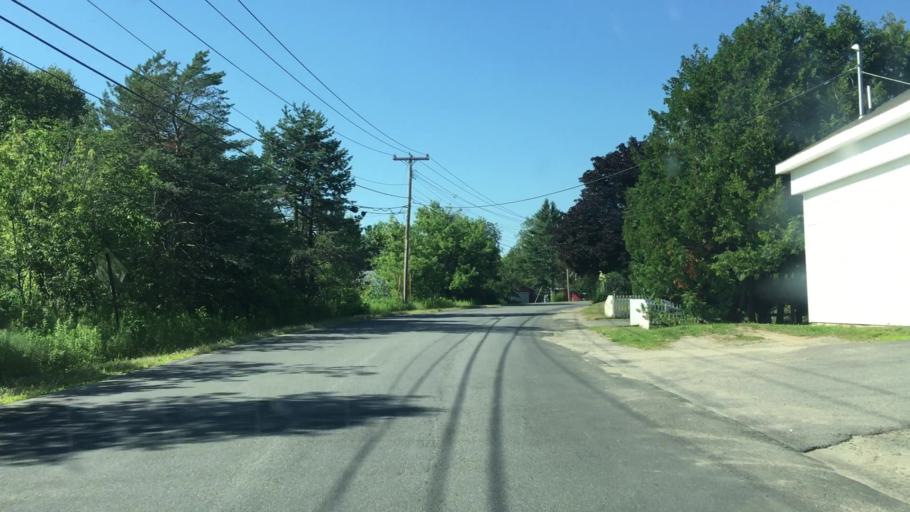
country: US
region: Maine
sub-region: Penobscot County
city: Howland
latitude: 45.2385
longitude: -68.6499
